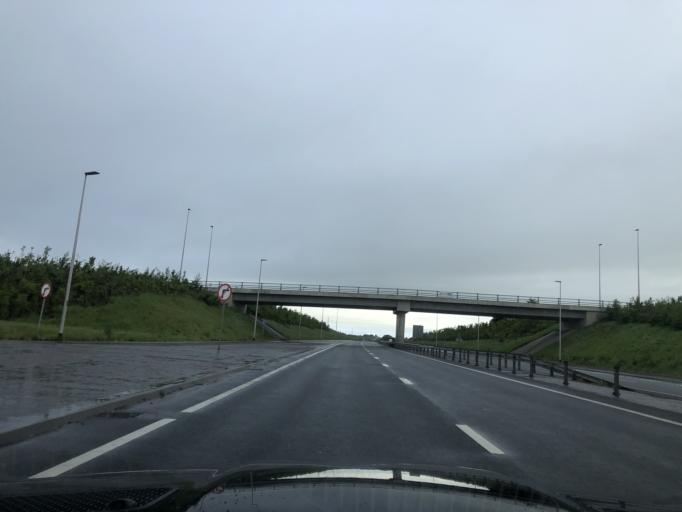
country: GB
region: Northern Ireland
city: Dunloy
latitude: 54.9840
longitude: -6.3485
